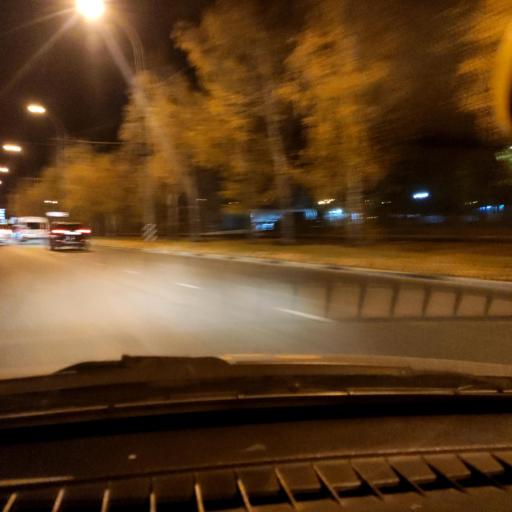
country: RU
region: Samara
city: Tol'yatti
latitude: 53.4984
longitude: 49.2869
